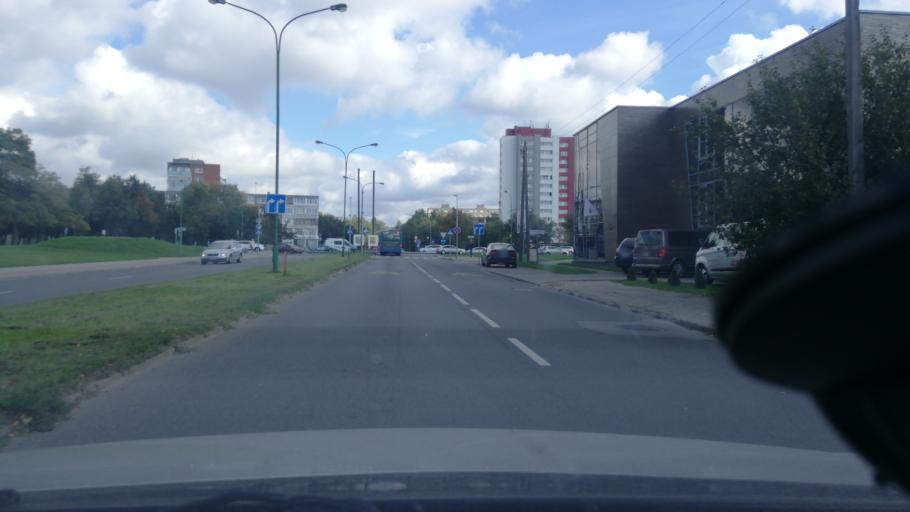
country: LT
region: Klaipedos apskritis
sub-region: Klaipeda
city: Klaipeda
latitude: 55.6802
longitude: 21.1631
